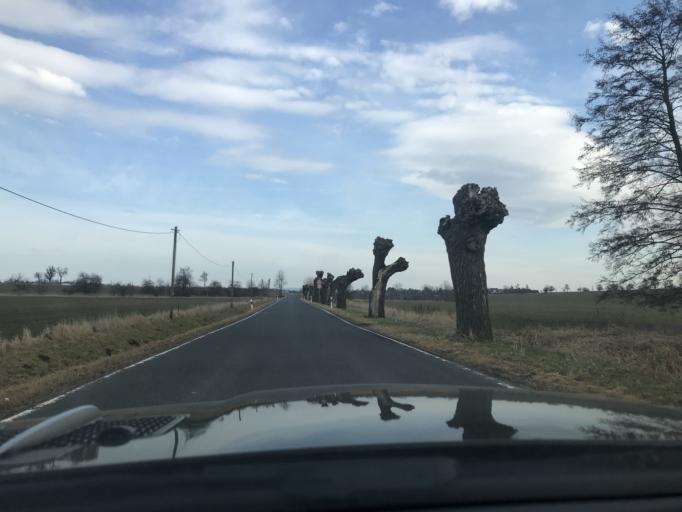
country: DE
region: Thuringia
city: Oberdorla
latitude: 51.1900
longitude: 10.4228
